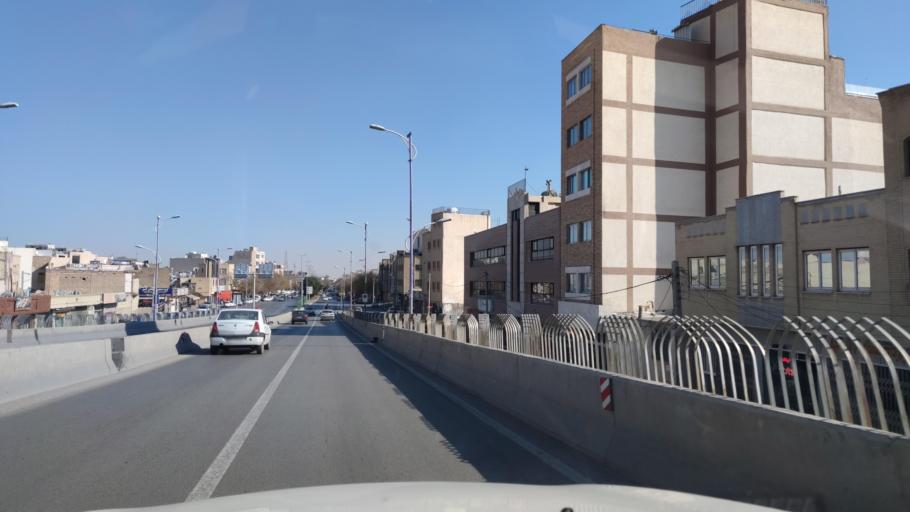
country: IR
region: Isfahan
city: Isfahan
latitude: 32.6790
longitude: 51.6737
